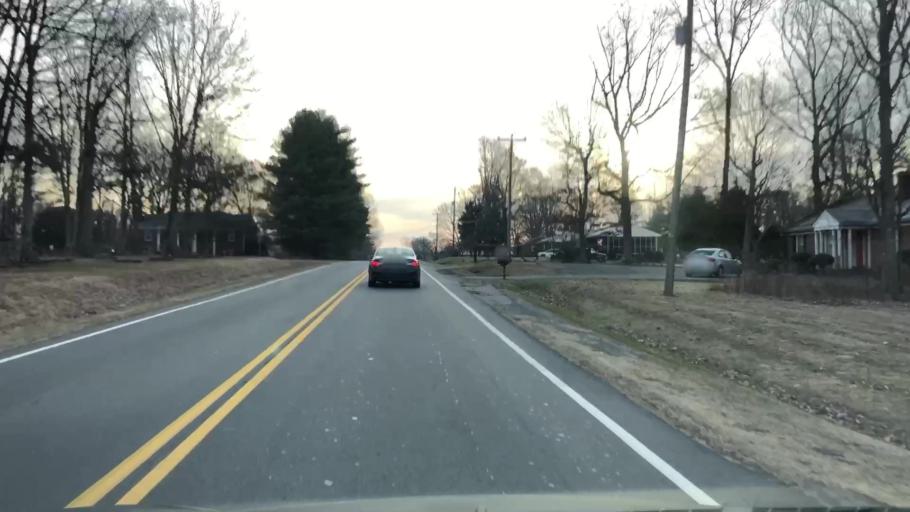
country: US
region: Virginia
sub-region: Campbell County
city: Timberlake
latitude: 37.3362
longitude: -79.2692
